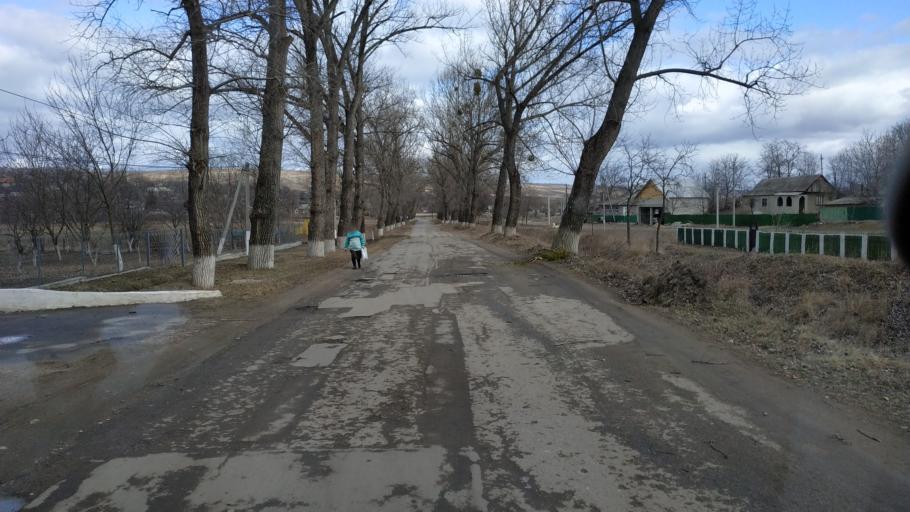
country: MD
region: Calarasi
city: Calarasi
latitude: 47.1283
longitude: 28.3104
